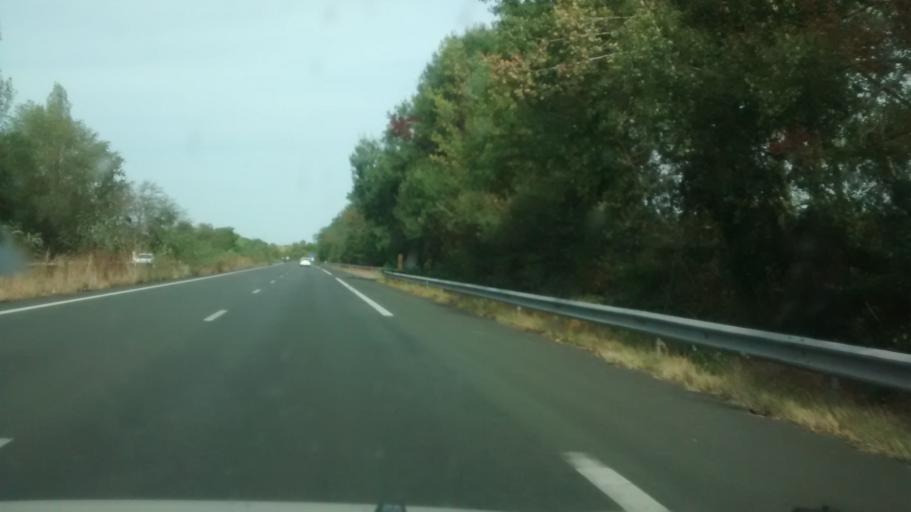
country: FR
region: Aquitaine
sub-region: Departement du Lot-et-Garonne
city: Meilhan-sur-Garonne
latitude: 44.4688
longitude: 0.0581
